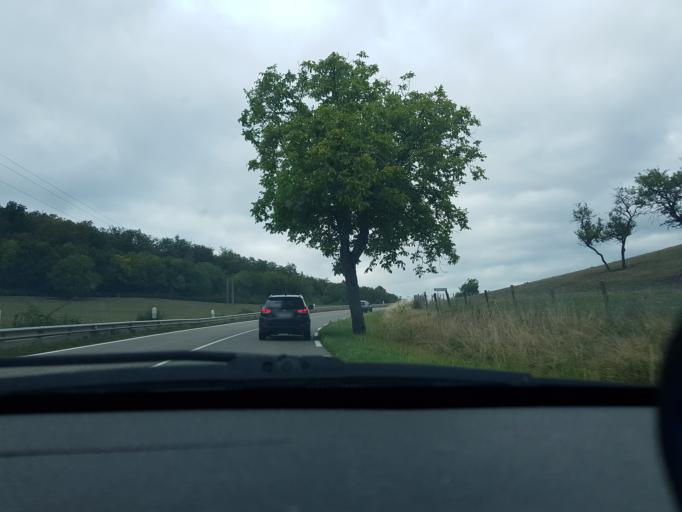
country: FR
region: Lorraine
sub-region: Departement de la Moselle
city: Chateau-Salins
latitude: 48.8842
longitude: 6.5371
